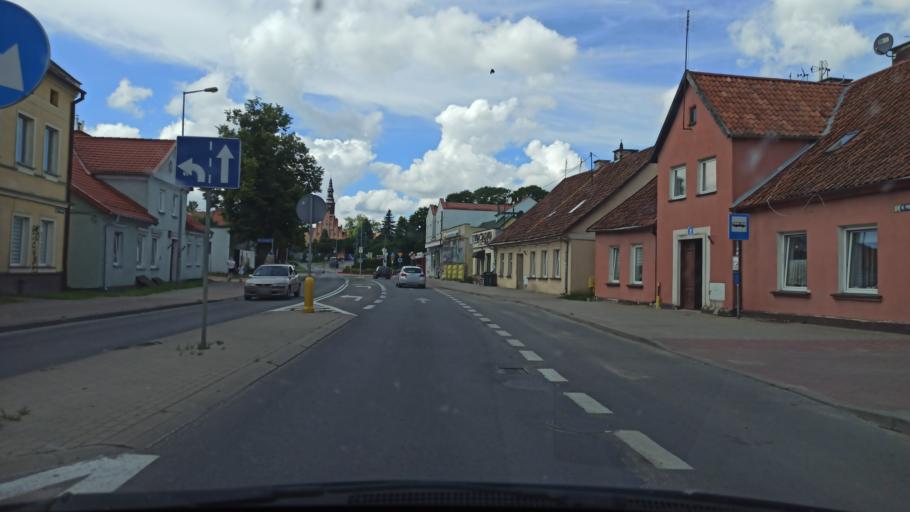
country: PL
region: Warmian-Masurian Voivodeship
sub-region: Powiat ostrodzki
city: Morag
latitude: 53.9108
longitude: 19.9319
